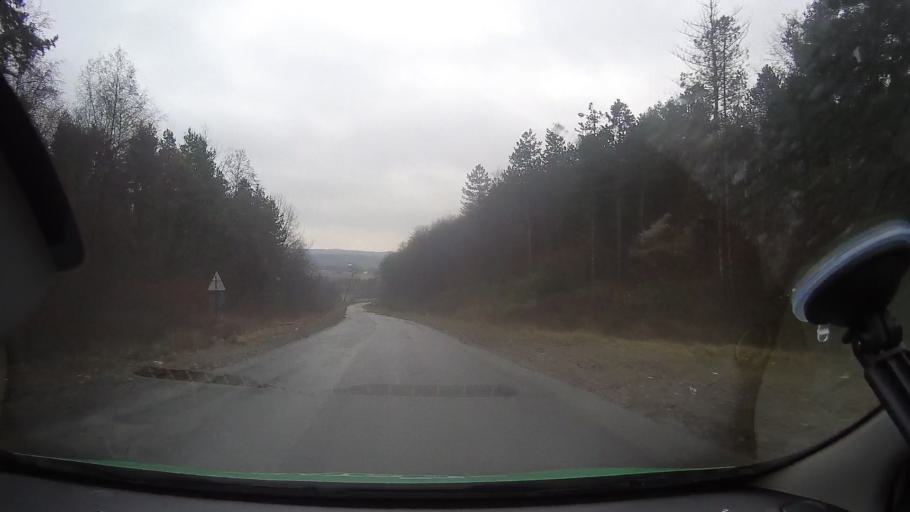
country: RO
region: Arad
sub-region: Comuna Halmagiu
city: Halmagiu
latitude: 46.2789
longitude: 22.5897
